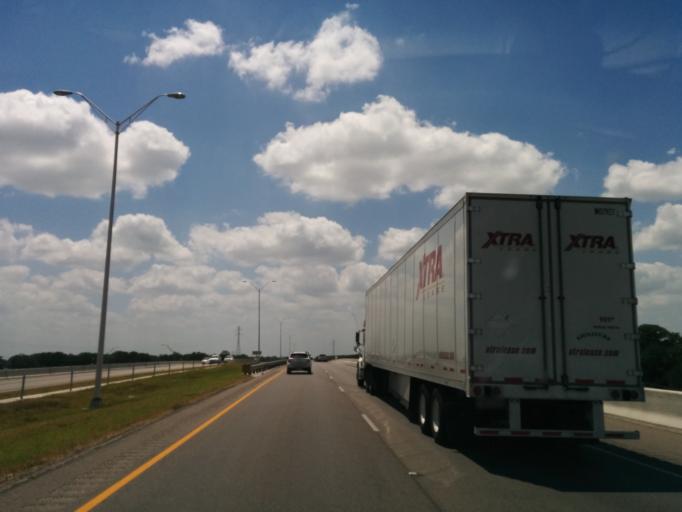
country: US
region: Texas
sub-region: Bastrop County
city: Bastrop
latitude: 30.1111
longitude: -97.3716
